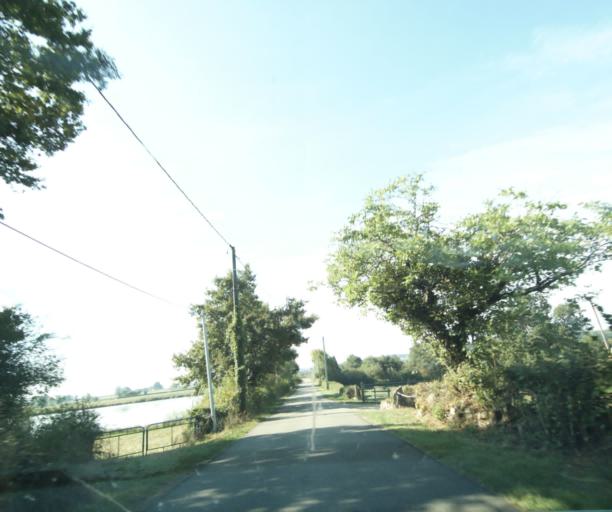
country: FR
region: Bourgogne
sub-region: Departement de Saone-et-Loire
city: Ciry-le-Noble
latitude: 46.5614
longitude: 4.3332
